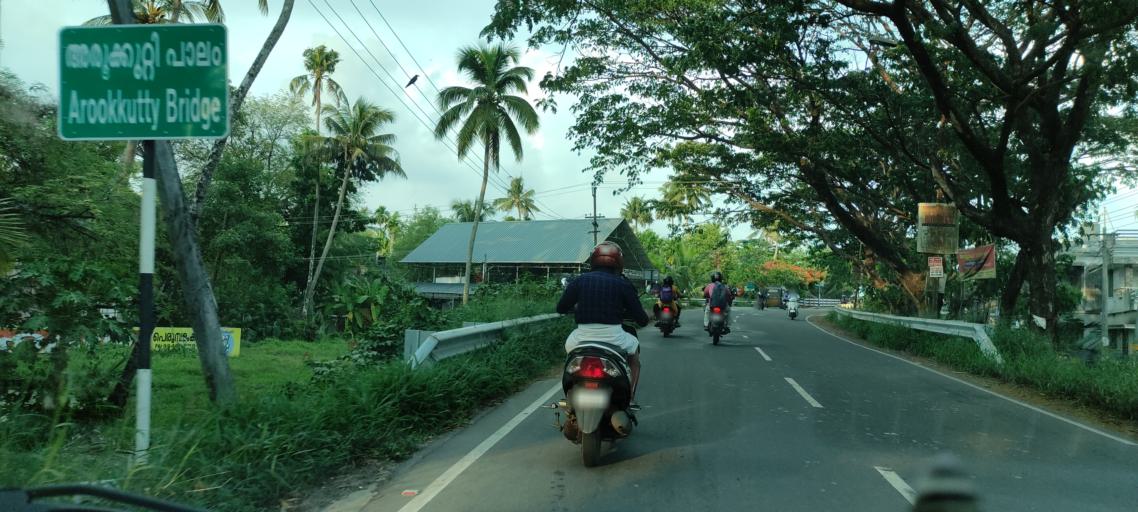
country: IN
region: Kerala
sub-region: Alappuzha
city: Arukutti
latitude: 9.8699
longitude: 76.3158
